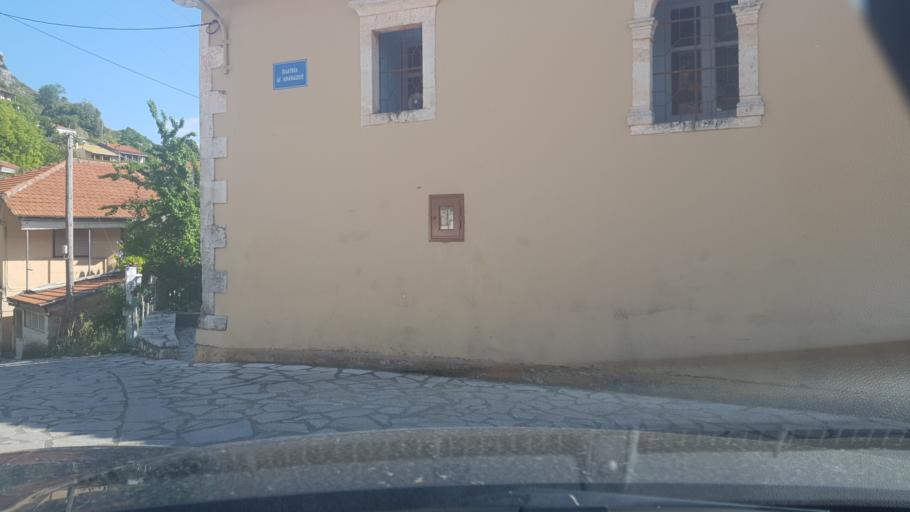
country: GR
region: Ionian Islands
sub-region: Lefkada
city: Nidri
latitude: 38.6901
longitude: 20.6455
